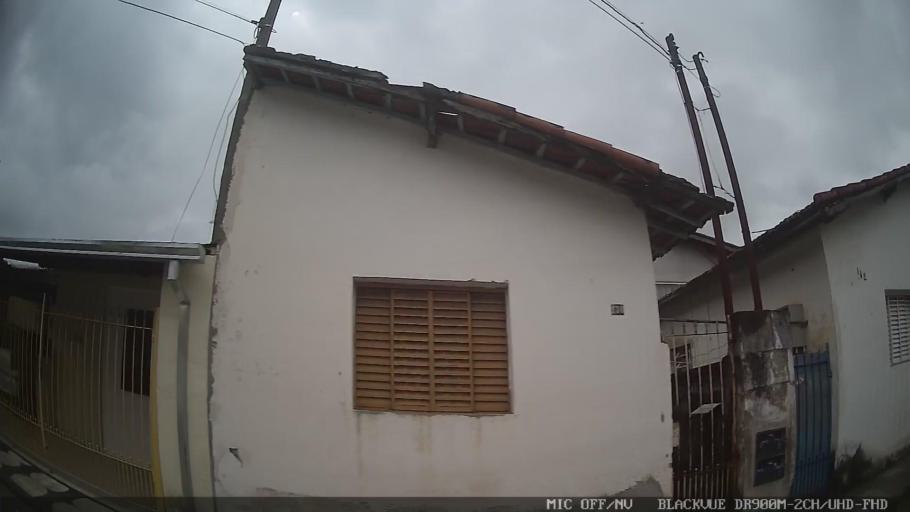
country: BR
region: Sao Paulo
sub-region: Mogi das Cruzes
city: Mogi das Cruzes
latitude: -23.5209
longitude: -46.2039
